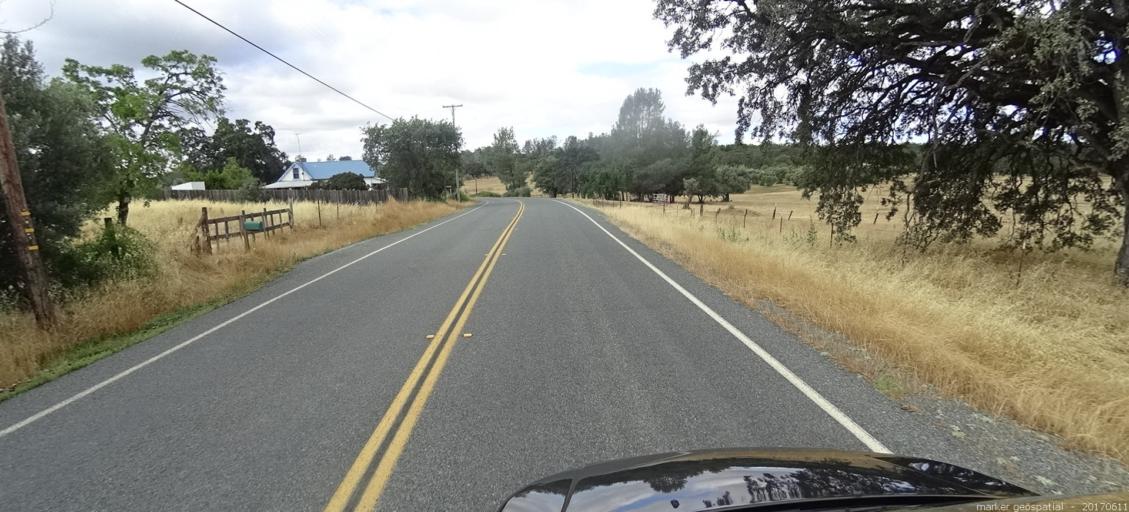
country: US
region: California
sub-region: Yuba County
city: Loma Rica
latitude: 39.3867
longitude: -121.4074
